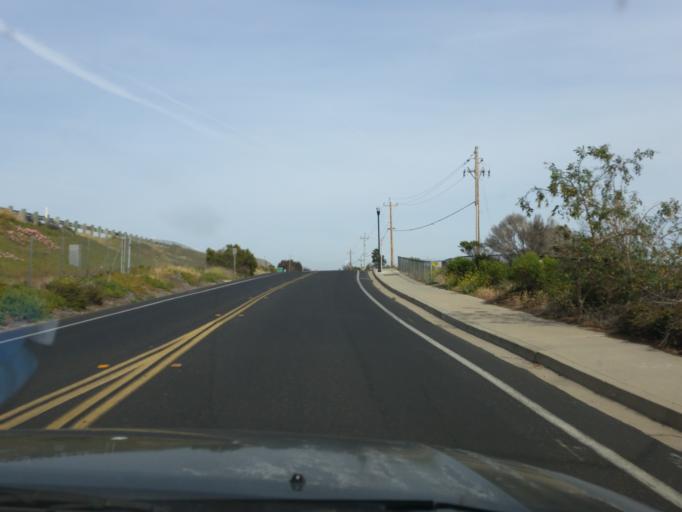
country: US
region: California
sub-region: San Luis Obispo County
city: Pismo Beach
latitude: 35.1521
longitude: -120.6589
